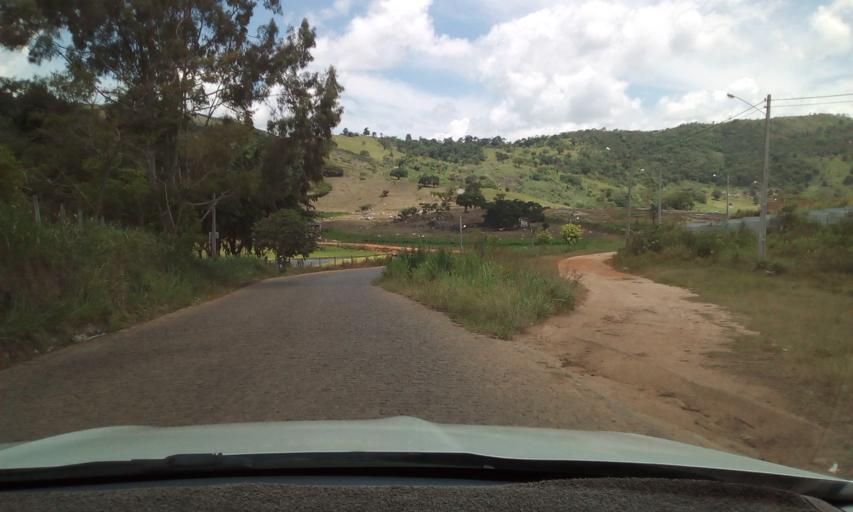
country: BR
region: Pernambuco
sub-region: Bonito
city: Bonito
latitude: -8.4833
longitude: -35.7302
